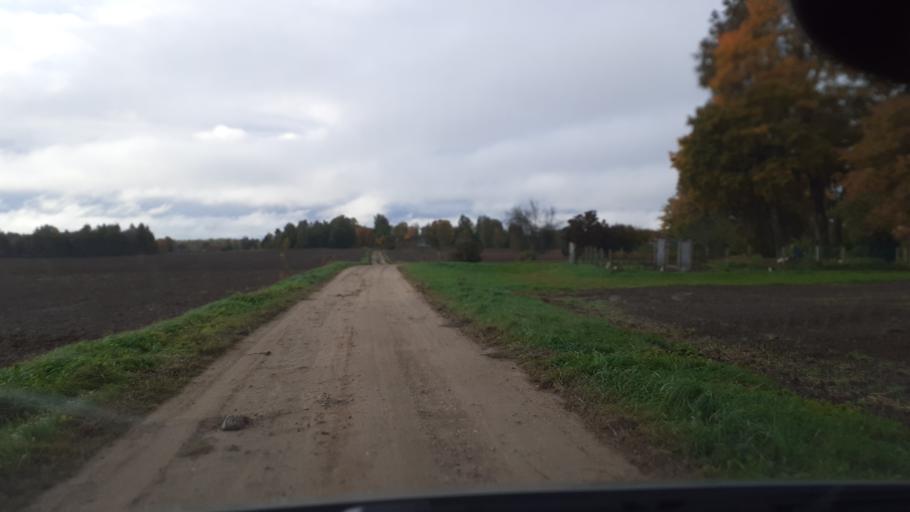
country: LV
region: Kuldigas Rajons
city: Kuldiga
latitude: 56.9774
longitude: 21.9399
